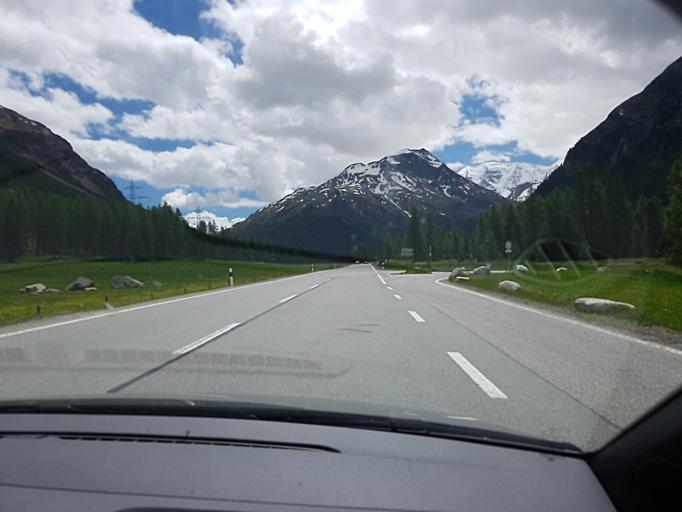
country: CH
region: Grisons
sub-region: Maloja District
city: Pontresina
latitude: 46.4713
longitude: 9.9270
